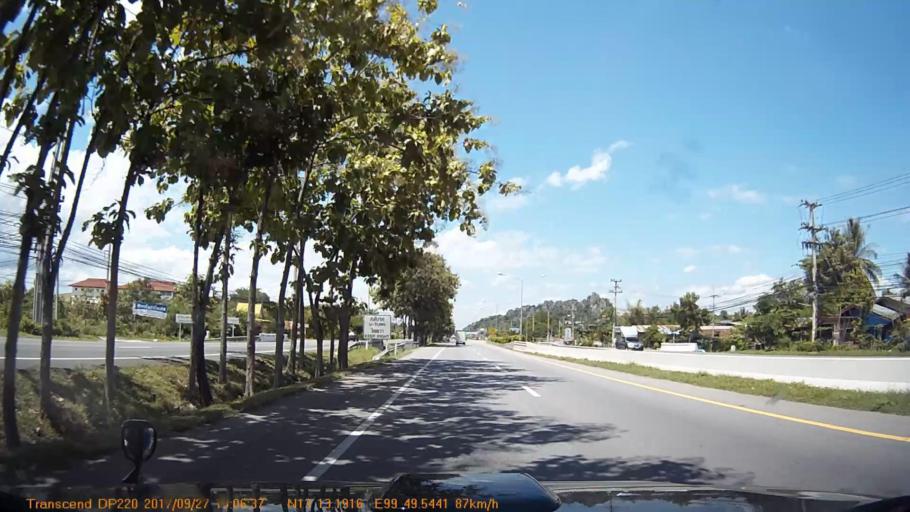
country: TH
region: Phetchaburi
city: Khao Yoi
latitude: 13.2200
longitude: 99.8257
